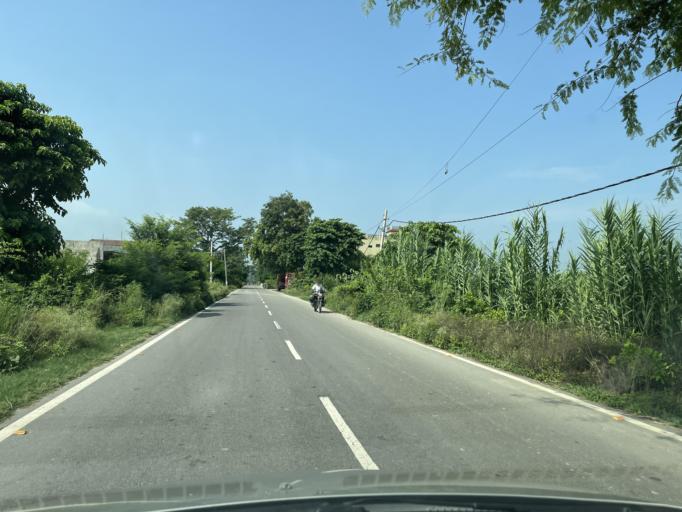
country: IN
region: Uttarakhand
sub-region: Udham Singh Nagar
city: Bazpur
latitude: 29.2011
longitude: 79.2042
